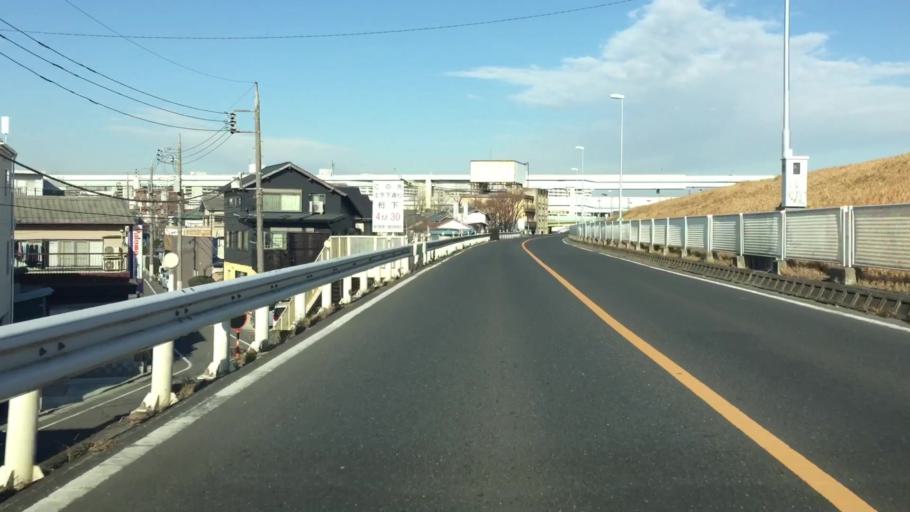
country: JP
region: Saitama
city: Kawaguchi
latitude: 35.7605
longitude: 139.7599
